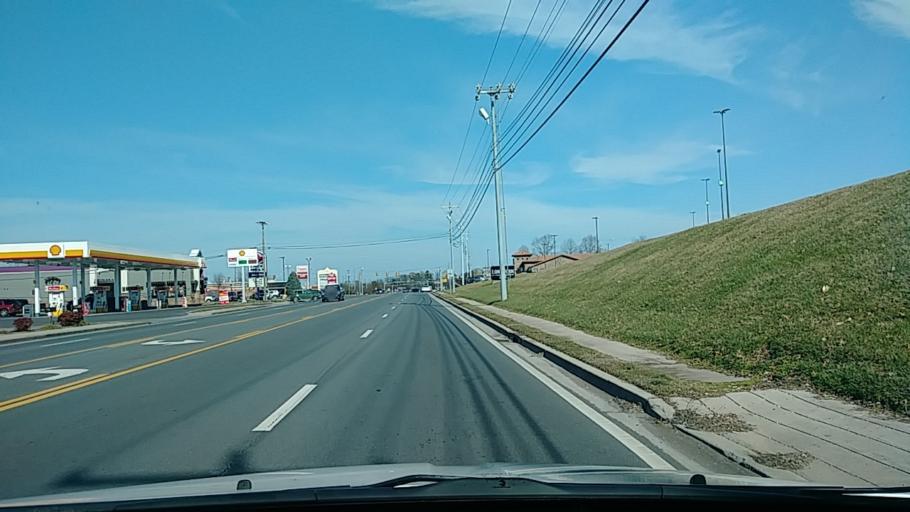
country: US
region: Tennessee
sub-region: Hamblen County
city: Morristown
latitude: 36.2217
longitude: -83.2637
